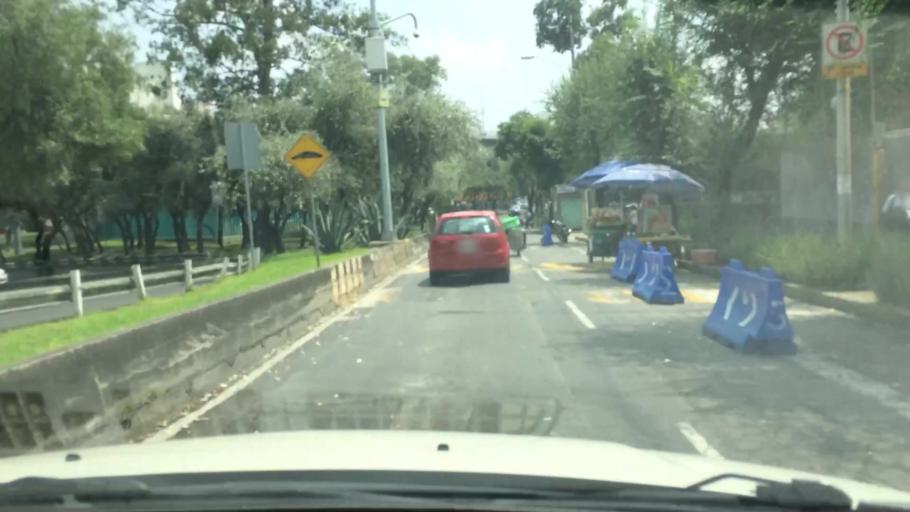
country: MX
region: Mexico City
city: Tlalpan
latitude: 19.2888
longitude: -99.1519
